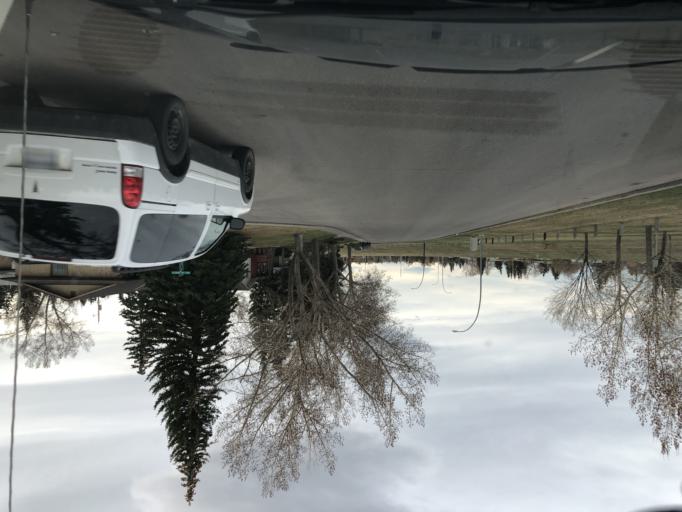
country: CA
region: Alberta
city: Calgary
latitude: 50.9392
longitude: -114.0331
